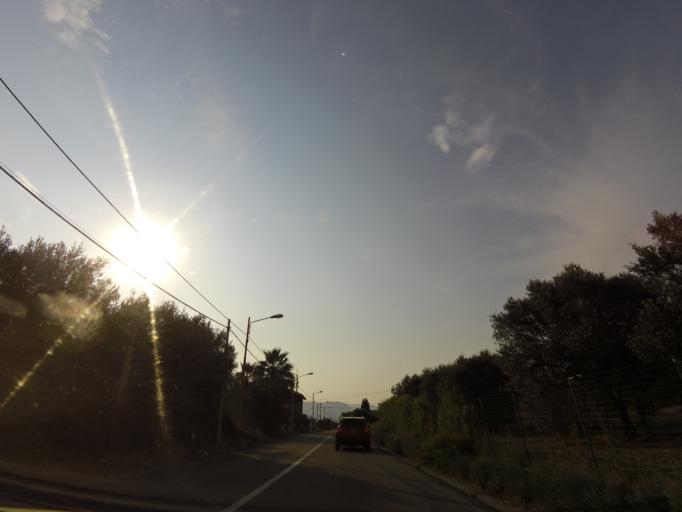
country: IT
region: Calabria
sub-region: Provincia di Reggio Calabria
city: Monasterace
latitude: 38.4438
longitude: 16.5394
